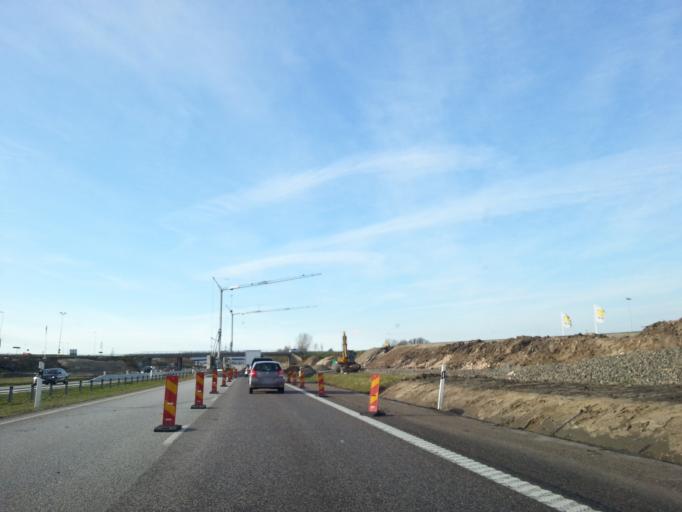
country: SE
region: Skane
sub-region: Angelholms Kommun
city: AEngelholm
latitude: 56.2500
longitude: 12.8987
